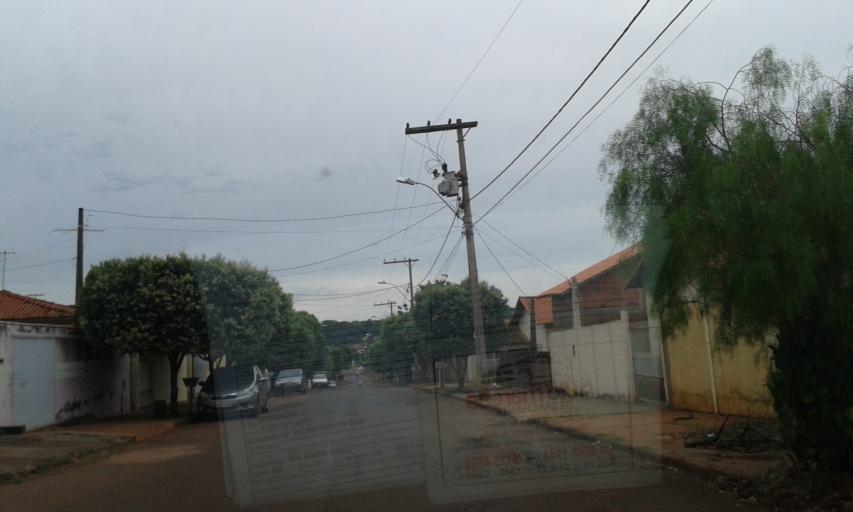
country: BR
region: Minas Gerais
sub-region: Ituiutaba
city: Ituiutaba
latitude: -18.9804
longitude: -49.4461
